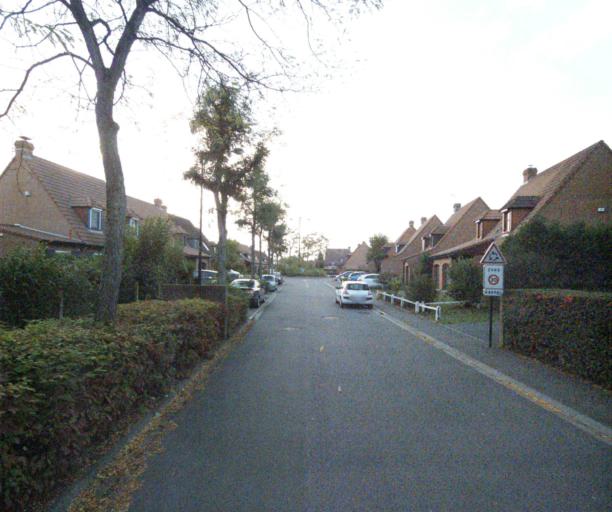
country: FR
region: Nord-Pas-de-Calais
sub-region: Departement du Nord
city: Sequedin
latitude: 50.6235
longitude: 2.9790
